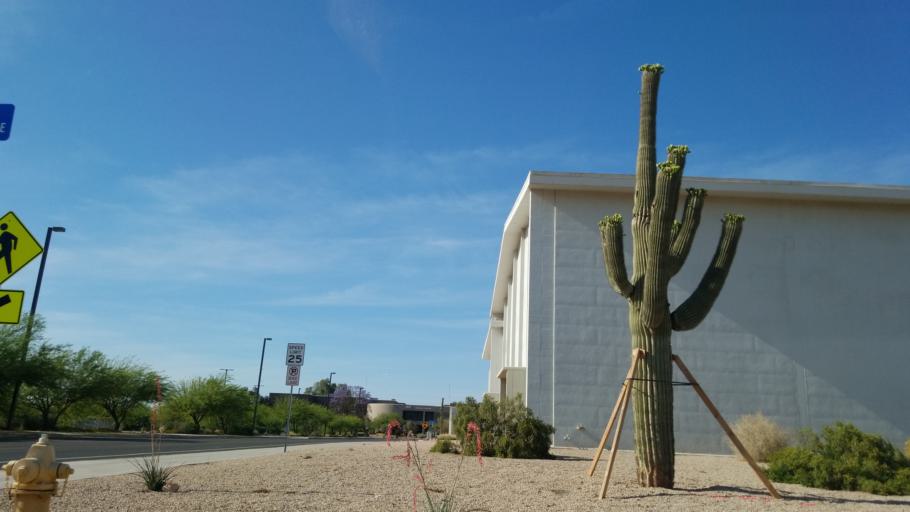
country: US
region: Arizona
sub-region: Maricopa County
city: Queen Creek
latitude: 33.3076
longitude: -111.6721
